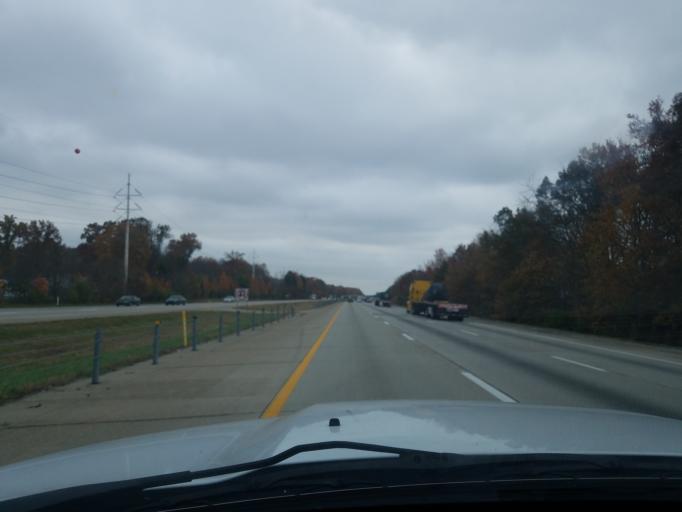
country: US
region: Kentucky
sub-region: Bullitt County
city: Hillview
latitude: 38.0835
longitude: -85.7007
